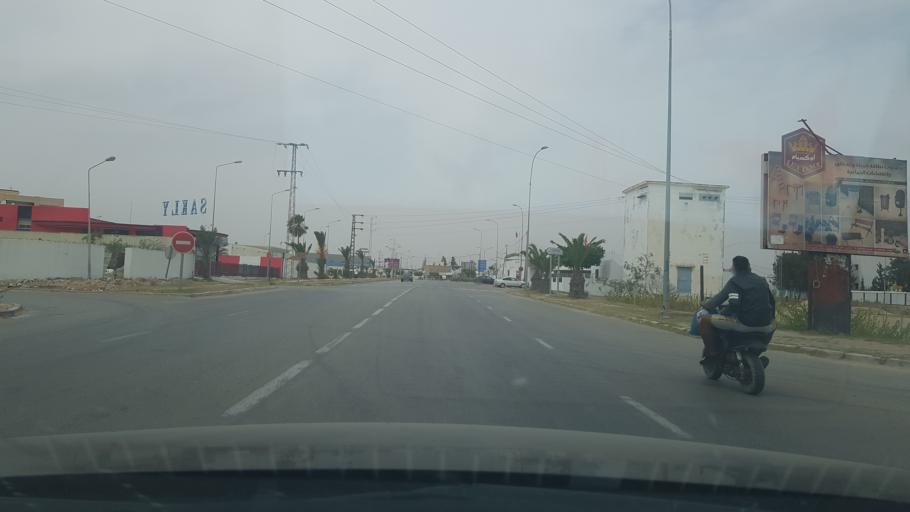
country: TN
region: Safaqis
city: Al Qarmadah
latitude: 34.8345
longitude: 10.7648
